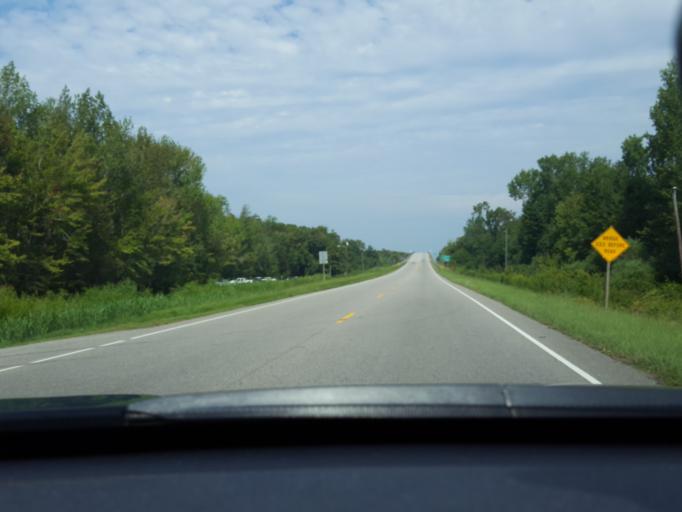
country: US
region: North Carolina
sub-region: Washington County
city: Plymouth
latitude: 35.9111
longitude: -76.7184
